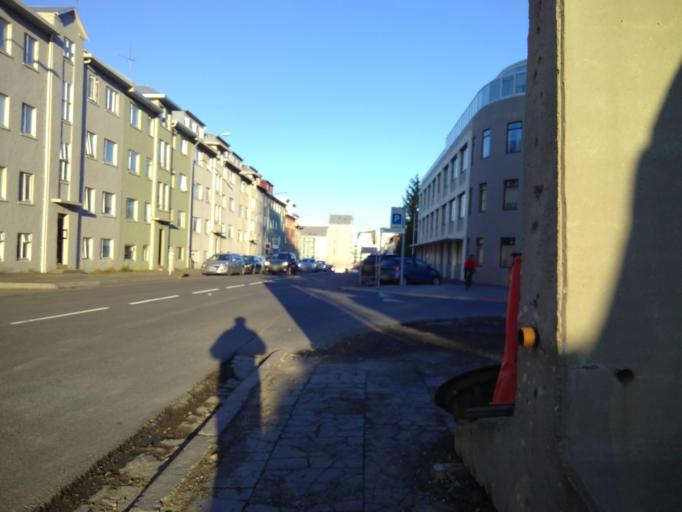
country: IS
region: Capital Region
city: Reykjavik
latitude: 64.1439
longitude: -21.9100
